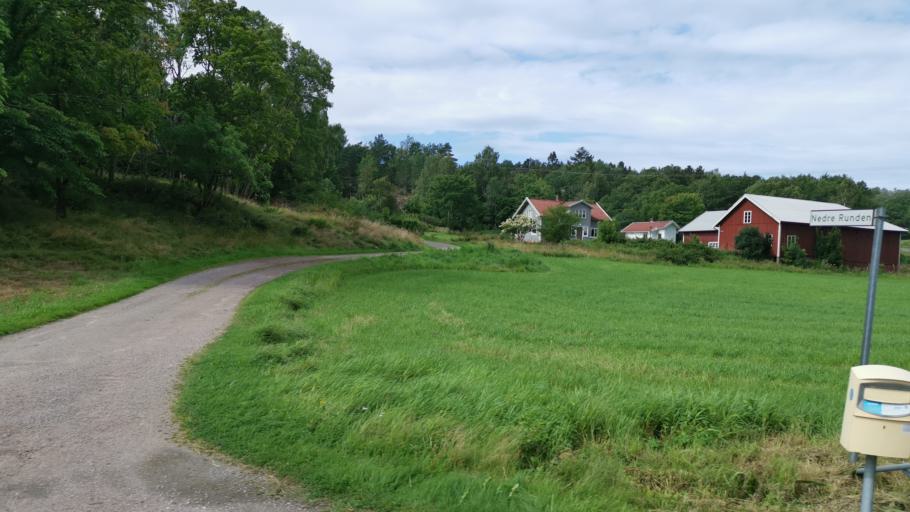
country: SE
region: Vaestra Goetaland
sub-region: Lysekils Kommun
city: Brastad
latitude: 58.4668
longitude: 11.4594
